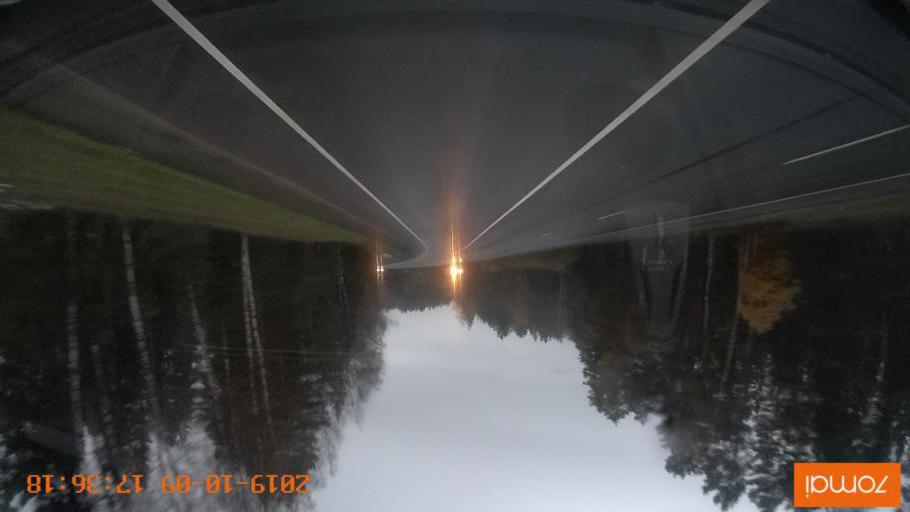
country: RU
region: Ivanovo
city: Bogorodskoye
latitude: 57.0804
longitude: 40.9979
